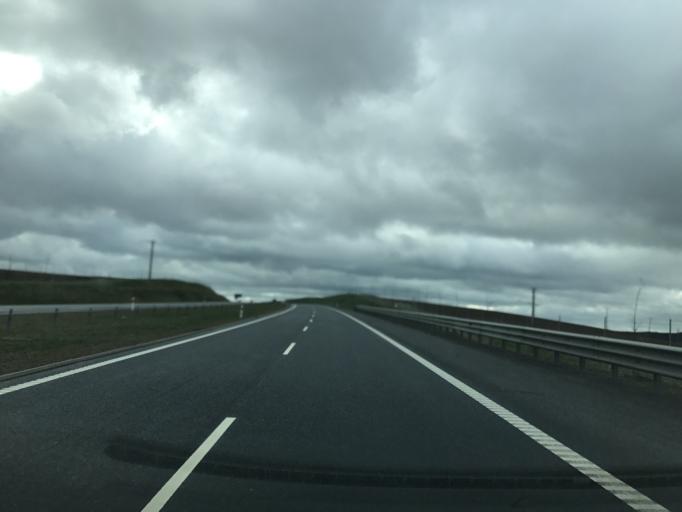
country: PL
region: Warmian-Masurian Voivodeship
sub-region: Powiat olsztynski
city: Olsztynek
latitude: 53.5984
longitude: 20.2699
